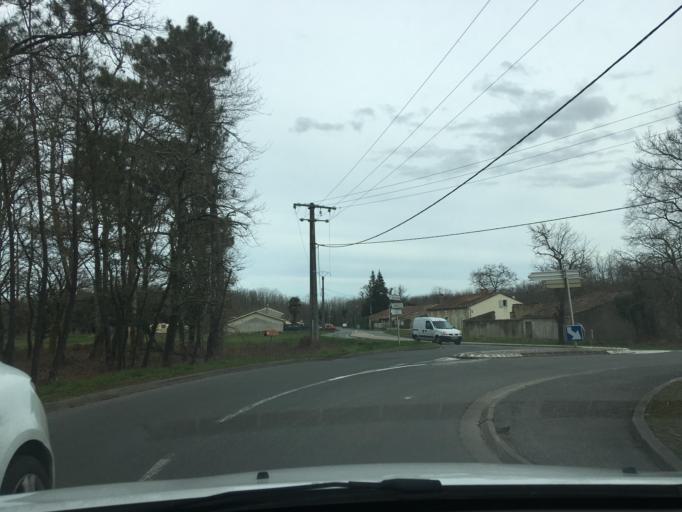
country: FR
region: Aquitaine
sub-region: Departement de la Gironde
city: Saint-Sauveur
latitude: 45.2196
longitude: -0.8693
